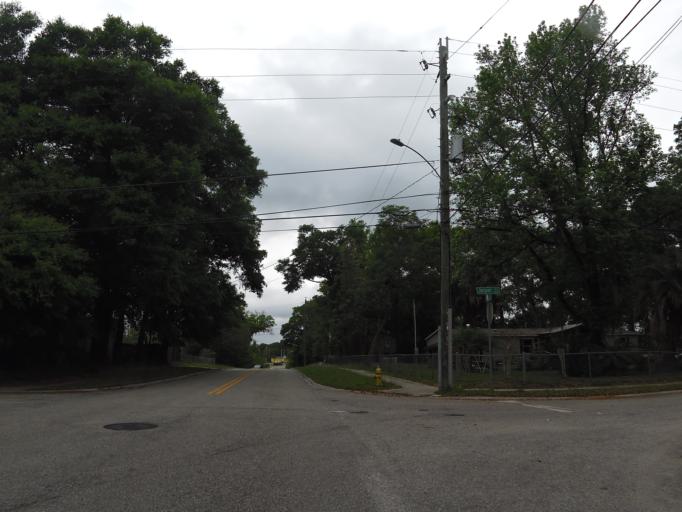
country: US
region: Florida
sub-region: Duval County
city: Jacksonville
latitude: 30.3221
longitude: -81.5663
